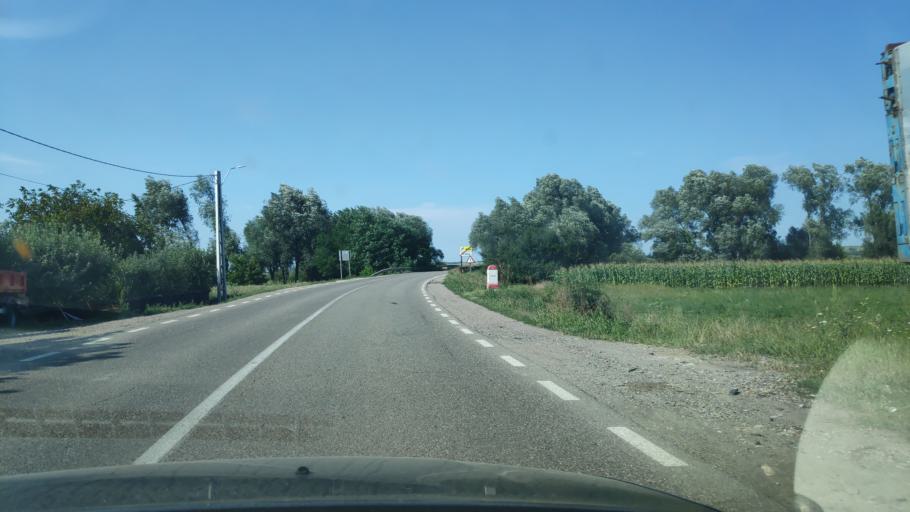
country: RO
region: Suceava
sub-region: Comuna Fantana Mare
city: Fantana Mare
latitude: 47.3836
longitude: 26.3146
